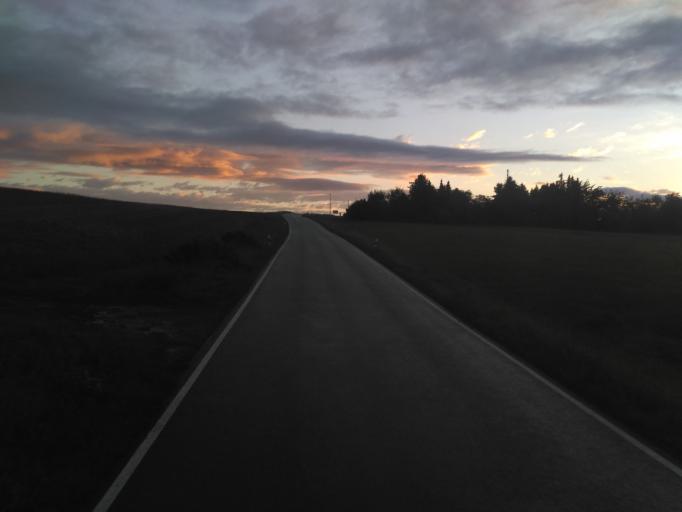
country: DE
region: Saxony
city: Durrrohrsdorf
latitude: 51.0375
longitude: 13.9759
